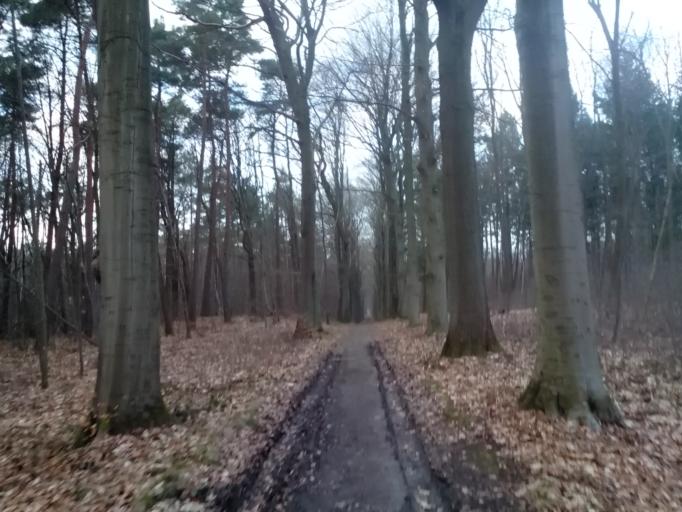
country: BE
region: Flanders
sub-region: Provincie Vlaams-Brabant
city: Oud-Heverlee
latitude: 50.8402
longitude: 4.6825
